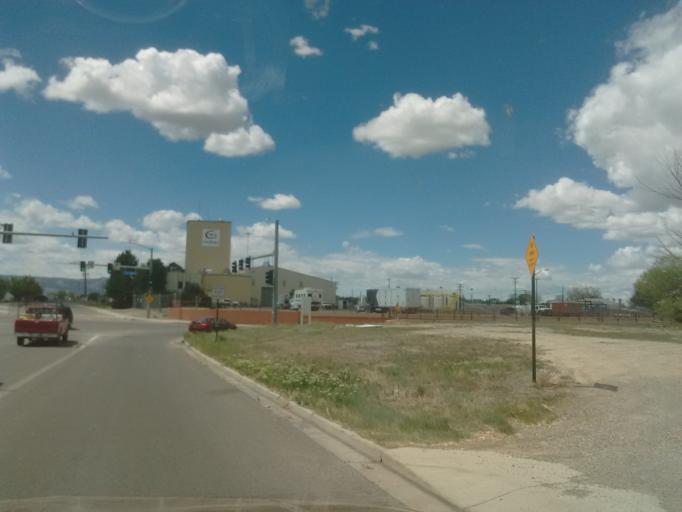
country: US
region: Colorado
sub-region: Mesa County
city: Fruitvale
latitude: 39.0757
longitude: -108.4959
